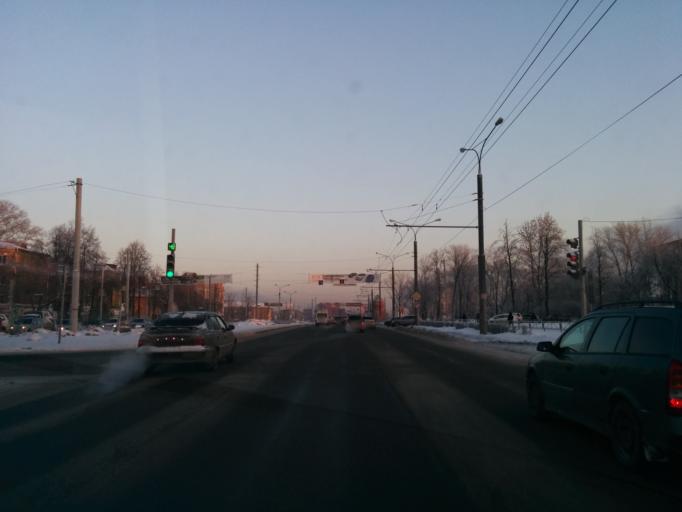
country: RU
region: Perm
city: Perm
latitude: 57.9853
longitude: 56.2525
